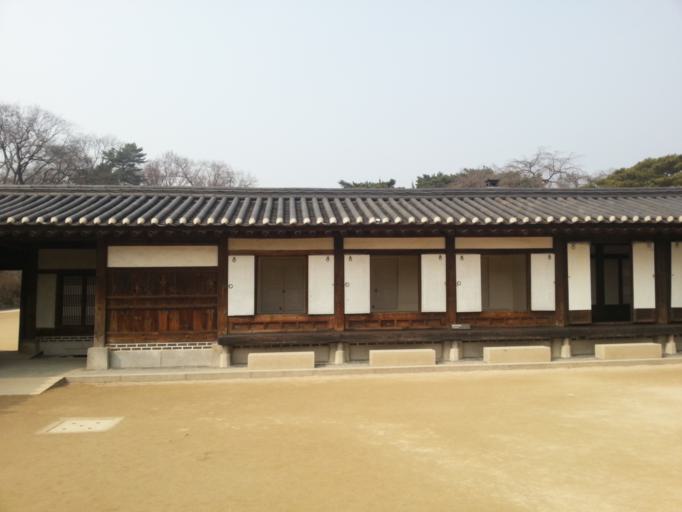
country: KR
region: Seoul
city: Seoul
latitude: 37.5786
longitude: 126.9934
